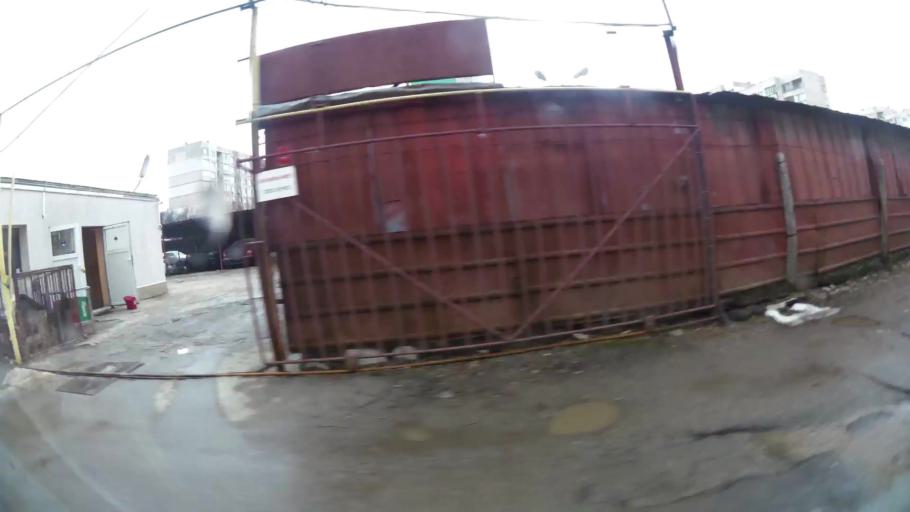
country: BG
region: Sofia-Capital
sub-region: Stolichna Obshtina
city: Sofia
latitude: 42.7329
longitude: 23.2936
